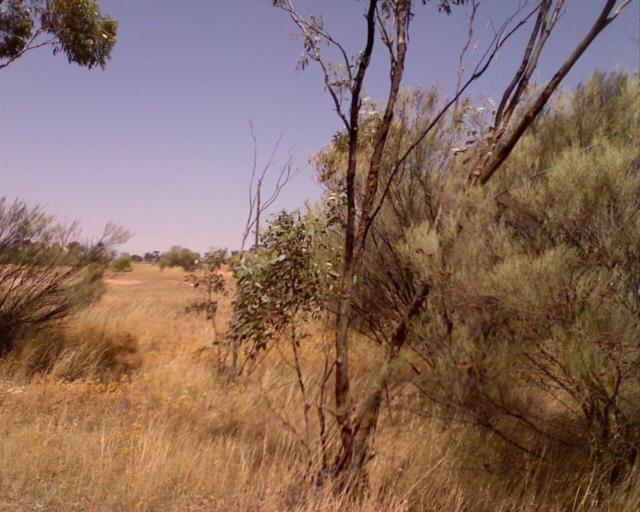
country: AU
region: Western Australia
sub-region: Merredin
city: Merredin
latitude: -30.9216
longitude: 118.2022
